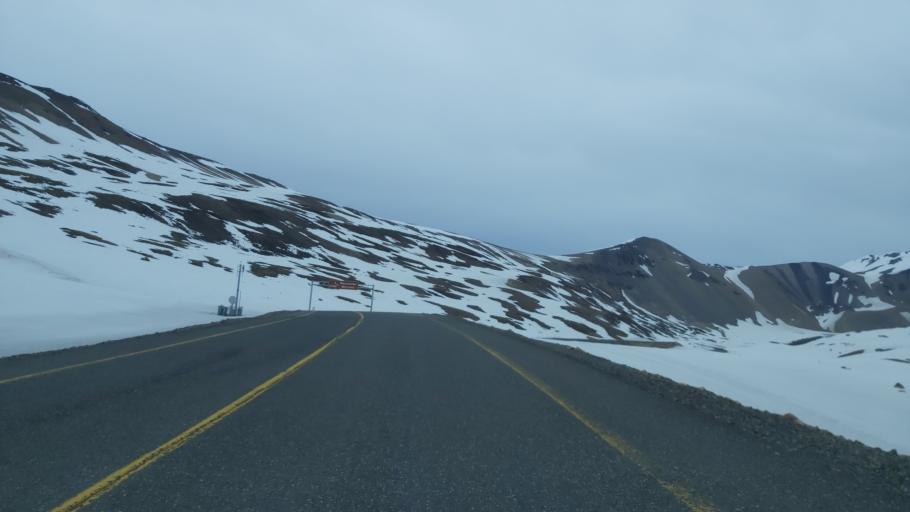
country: AR
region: Mendoza
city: Malargue
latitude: -35.9842
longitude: -70.3943
